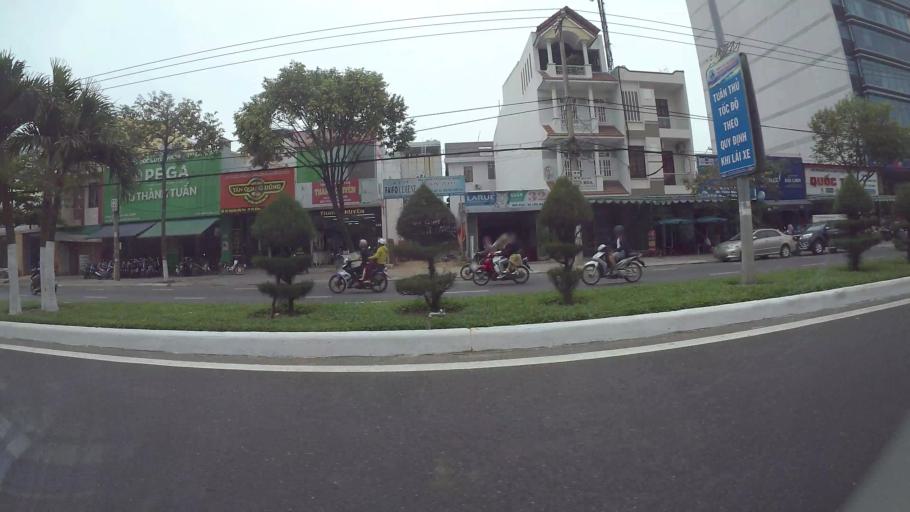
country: VN
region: Da Nang
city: Cam Le
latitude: 16.0352
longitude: 108.2097
